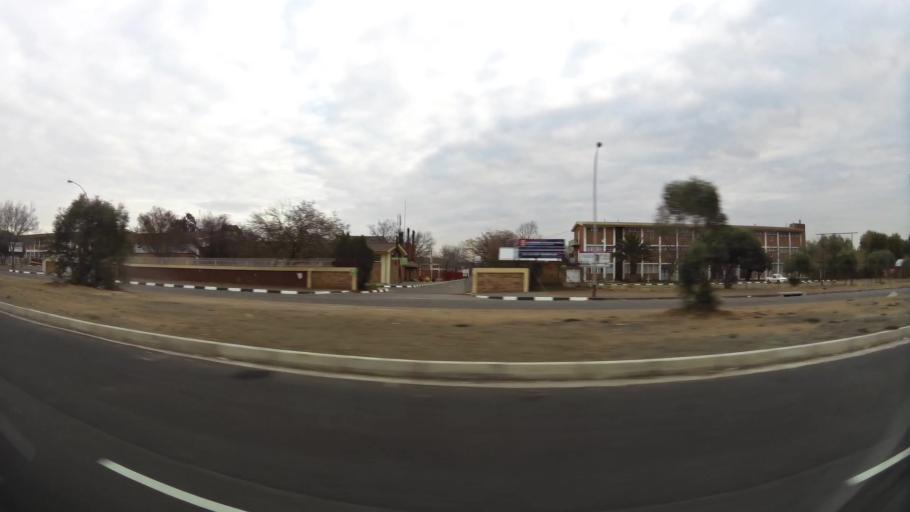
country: ZA
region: Orange Free State
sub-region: Mangaung Metropolitan Municipality
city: Bloemfontein
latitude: -29.1259
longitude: 26.1912
